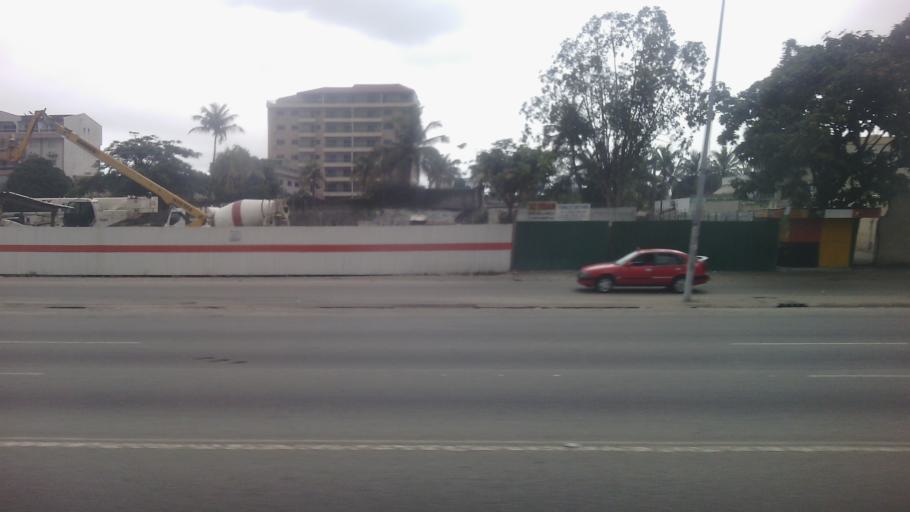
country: CI
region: Lagunes
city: Abidjan
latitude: 5.2932
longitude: -3.9762
